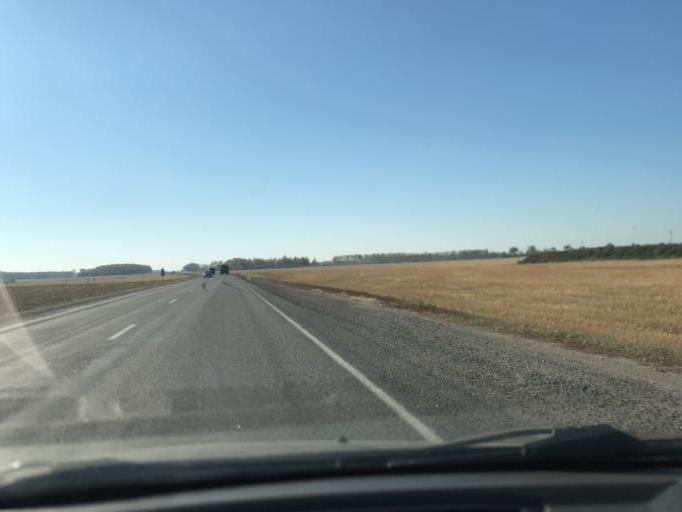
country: BY
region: Gomel
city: Rechytsa
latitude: 52.2641
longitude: 30.2473
